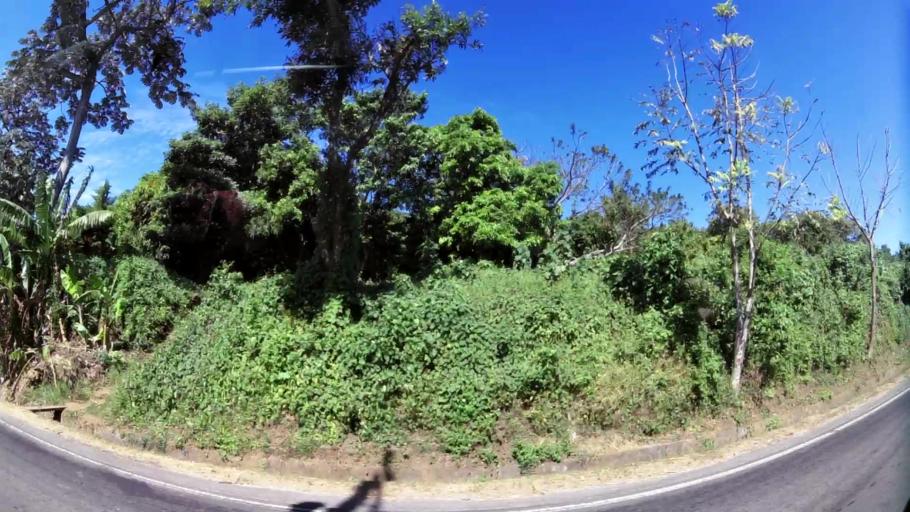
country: SV
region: Sonsonate
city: Juayua
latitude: 13.8374
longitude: -89.7635
